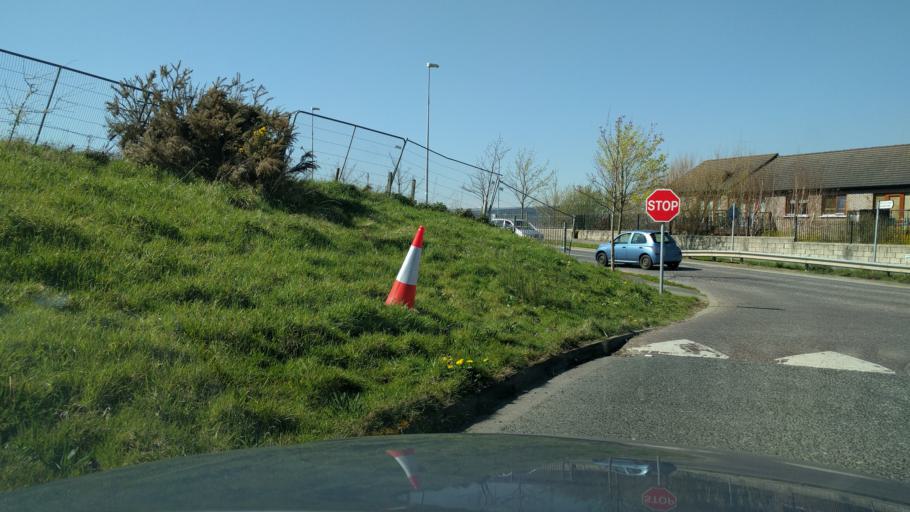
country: IE
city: Knocklyon
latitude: 53.2693
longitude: -6.3326
